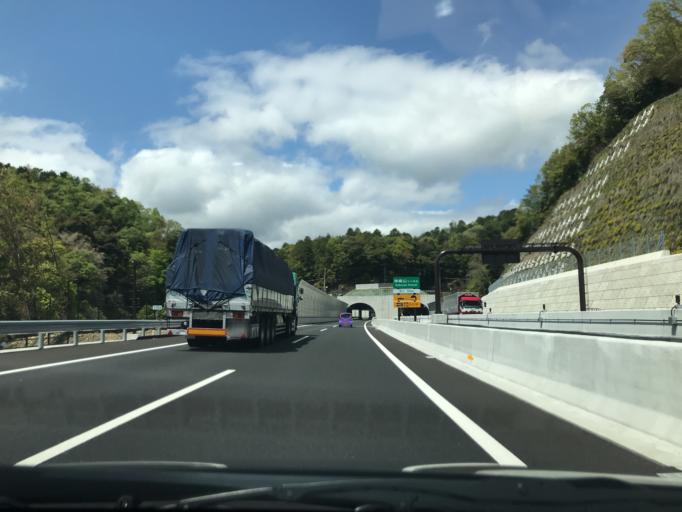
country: JP
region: Osaka
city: Takatsuki
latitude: 34.8926
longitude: 135.6088
